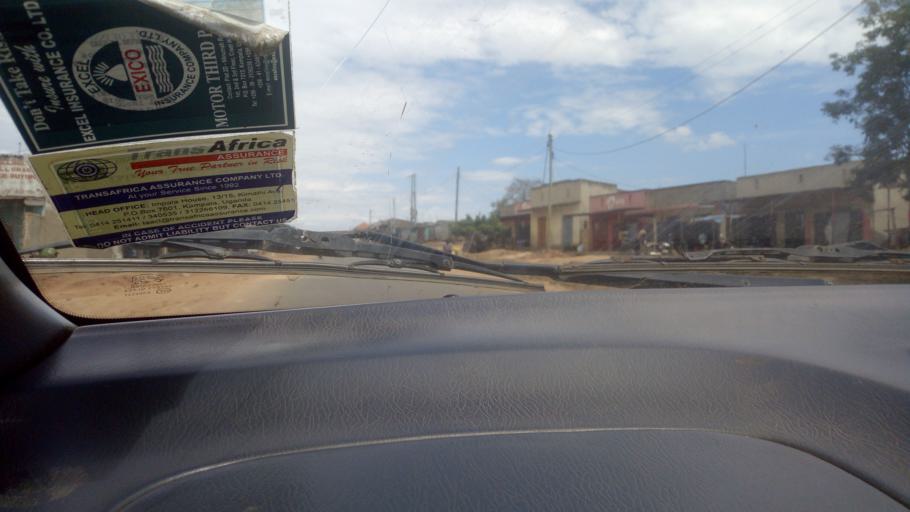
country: UG
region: Western Region
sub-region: Mbarara District
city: Bwizibwera
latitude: -0.4092
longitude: 30.5684
